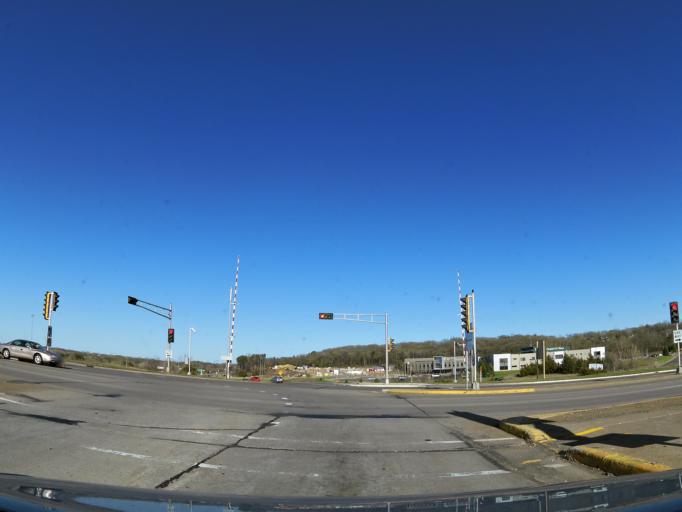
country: US
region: Wisconsin
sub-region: Saint Croix County
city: Hudson
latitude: 44.9621
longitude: -92.7216
